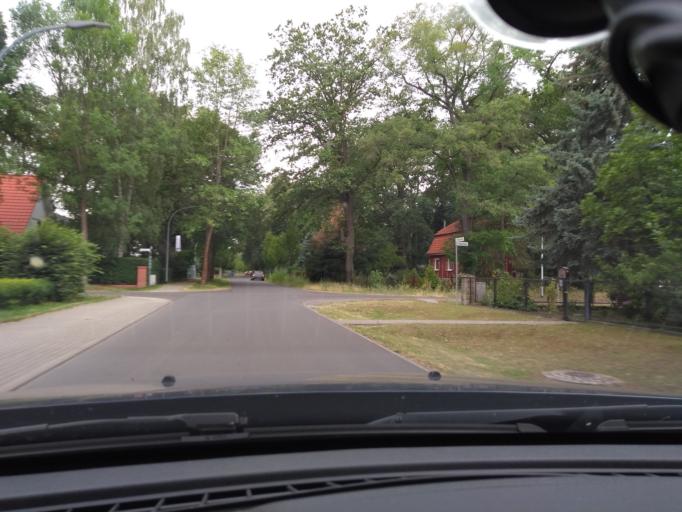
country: DE
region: Brandenburg
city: Dallgow-Doeberitz
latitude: 52.5593
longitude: 13.0570
